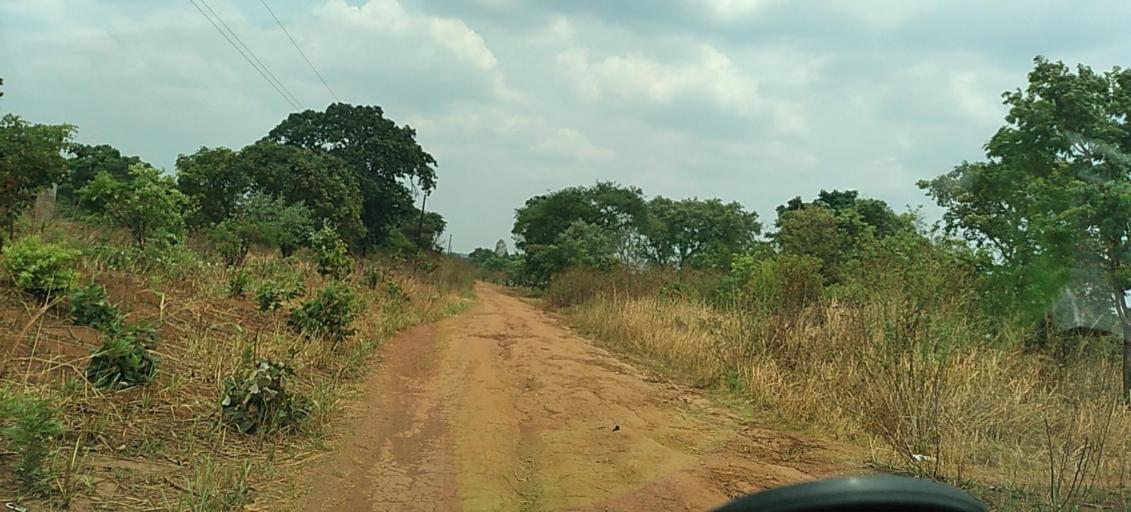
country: ZM
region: North-Western
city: Kansanshi
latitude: -12.0383
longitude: 26.3996
